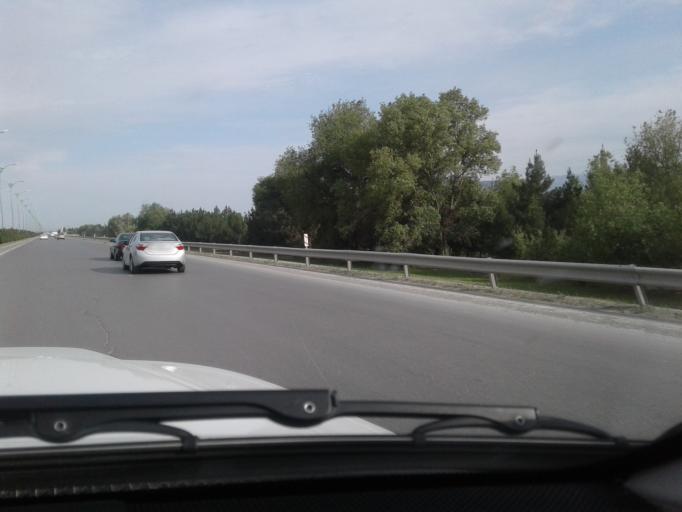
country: TM
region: Ahal
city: Abadan
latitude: 38.1485
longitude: 57.9855
